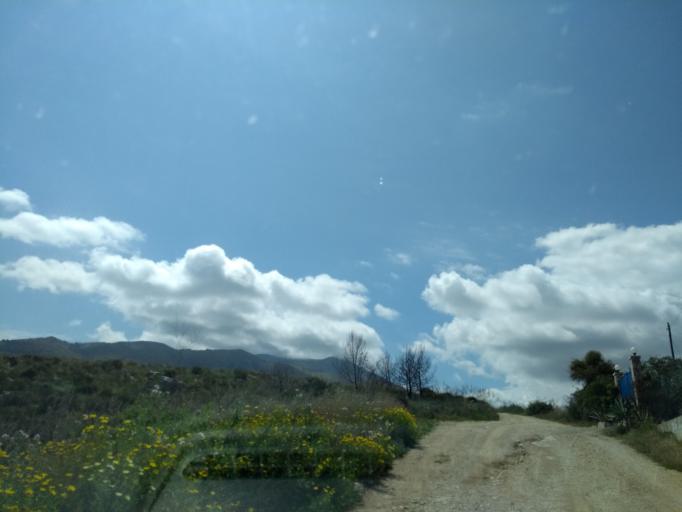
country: IT
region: Sicily
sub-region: Trapani
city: Castellammare del Golfo
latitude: 38.0501
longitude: 12.8487
